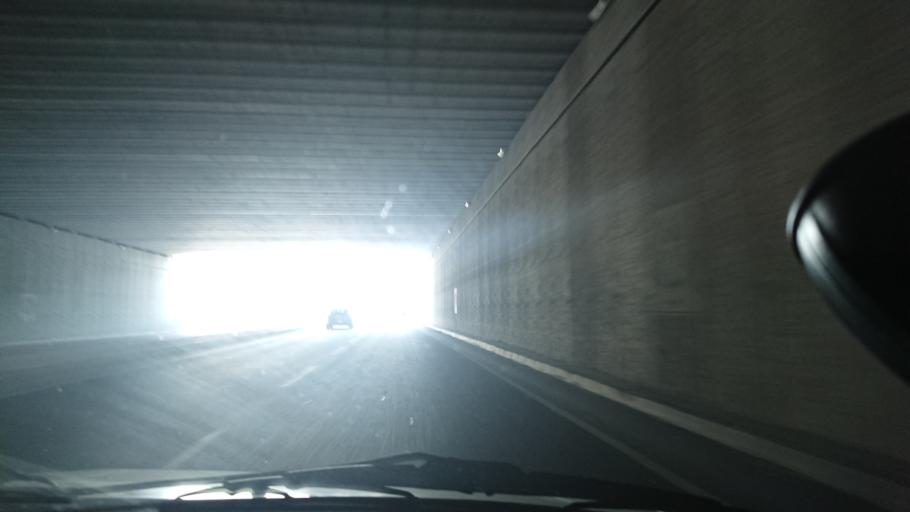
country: TR
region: Manisa
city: Turgutlu
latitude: 38.4908
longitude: 27.7057
